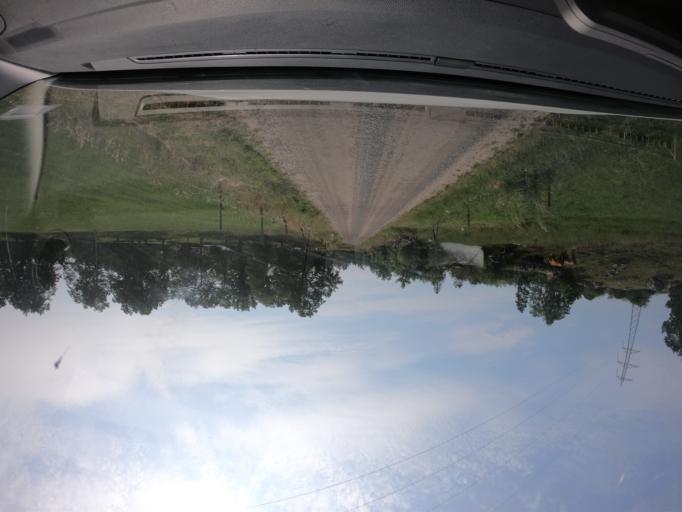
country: SE
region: Skane
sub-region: Hassleholms Kommun
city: Bjarnum
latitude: 56.2669
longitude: 13.6561
